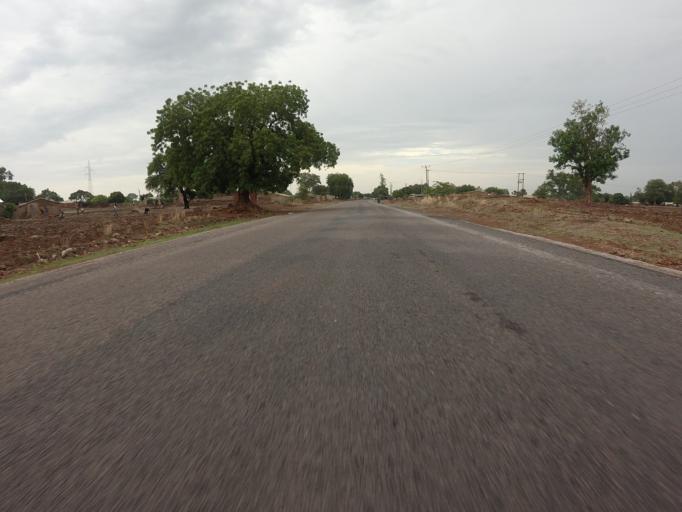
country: GH
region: Upper East
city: Bolgatanga
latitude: 10.8522
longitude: -0.6749
